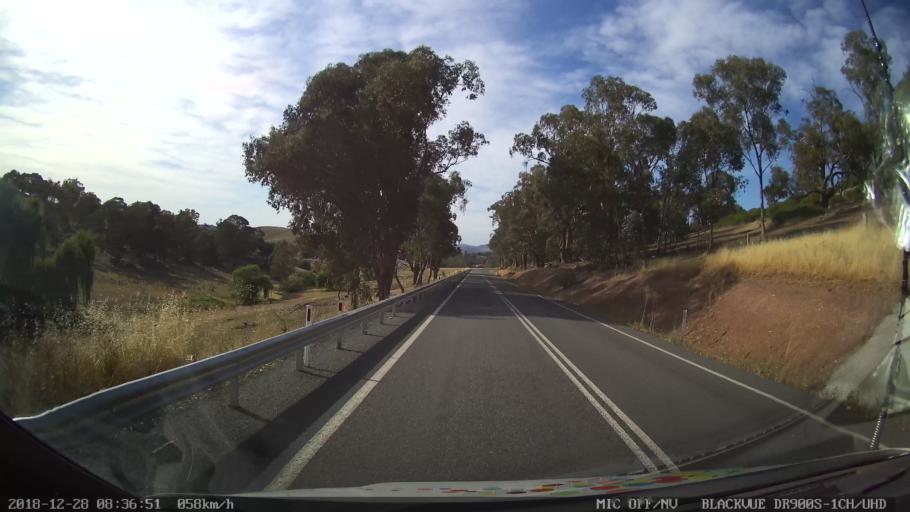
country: AU
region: New South Wales
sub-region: Blayney
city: Blayney
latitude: -33.9904
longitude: 149.3126
